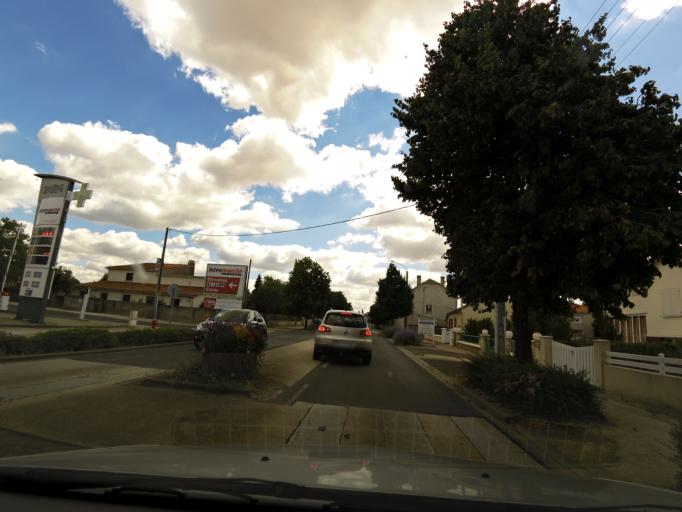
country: FR
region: Poitou-Charentes
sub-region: Departement des Deux-Sevres
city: Beauvoir-sur-Niort
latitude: 46.1847
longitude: -0.4739
